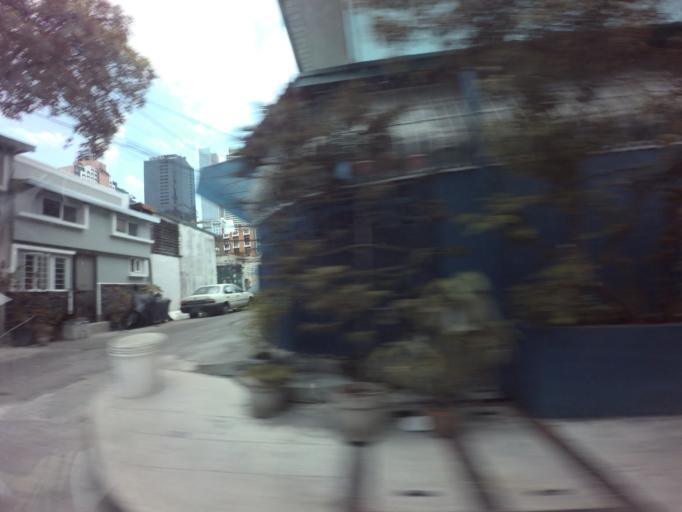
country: PH
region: Metro Manila
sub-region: Makati City
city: Makati City
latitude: 14.5646
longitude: 121.0328
